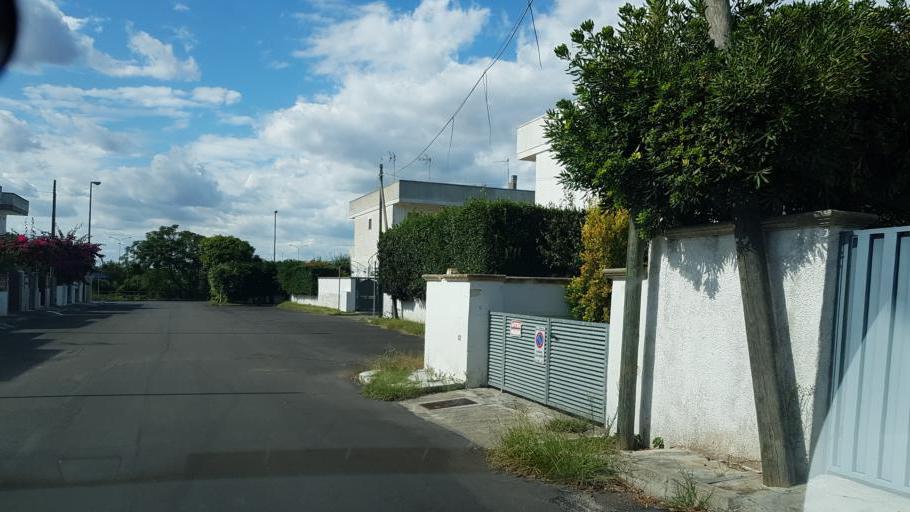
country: IT
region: Apulia
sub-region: Provincia di Lecce
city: Borgagne
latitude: 40.2750
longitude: 18.4263
